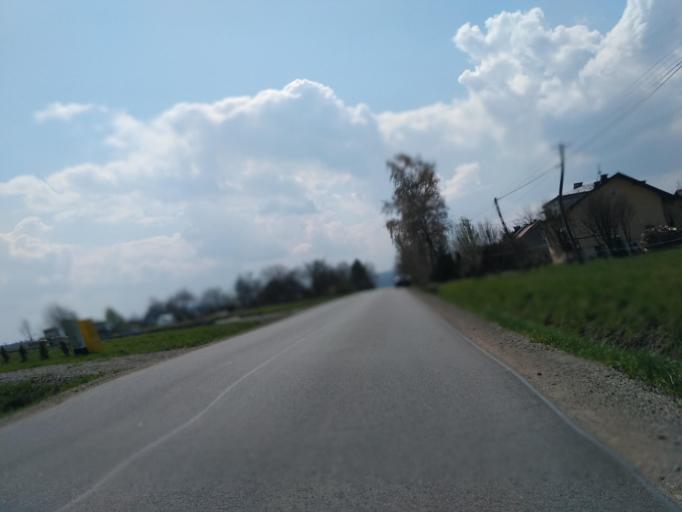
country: PL
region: Subcarpathian Voivodeship
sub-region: Powiat sanocki
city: Zarszyn
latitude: 49.5178
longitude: 21.9998
